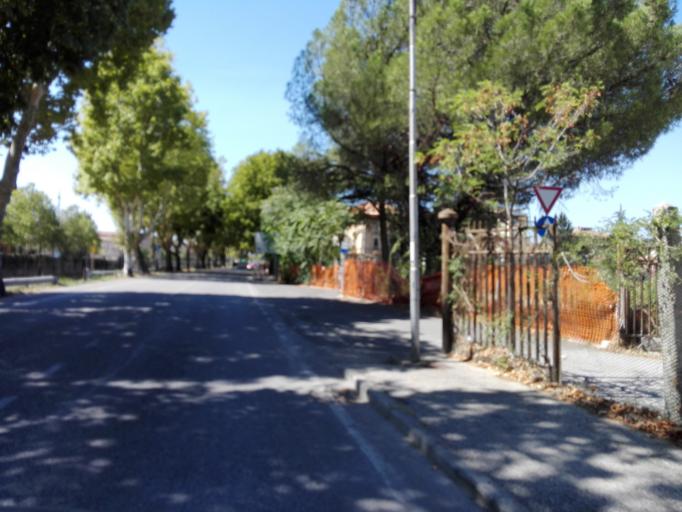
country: IT
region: Umbria
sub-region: Provincia di Perugia
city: Foligno
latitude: 42.9604
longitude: 12.7040
